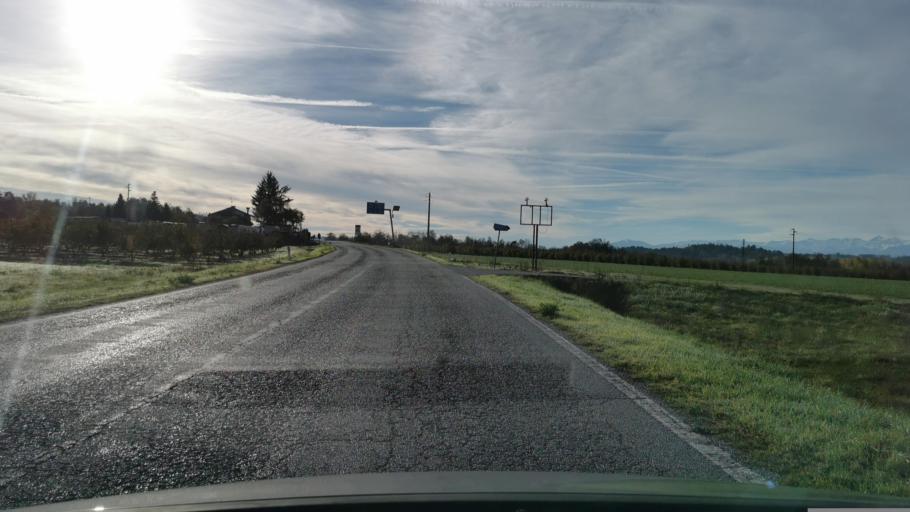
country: IT
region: Piedmont
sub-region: Provincia di Cuneo
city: Narzole
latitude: 44.6067
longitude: 7.8865
